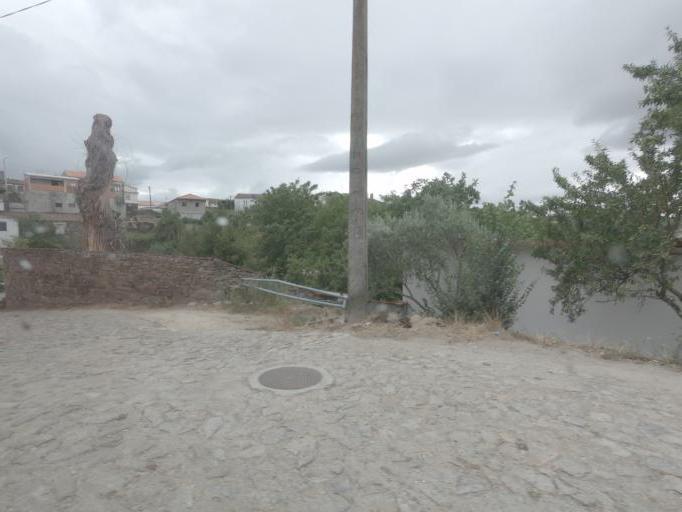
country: PT
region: Vila Real
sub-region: Sabrosa
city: Sabrosa
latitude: 41.2239
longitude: -7.5019
